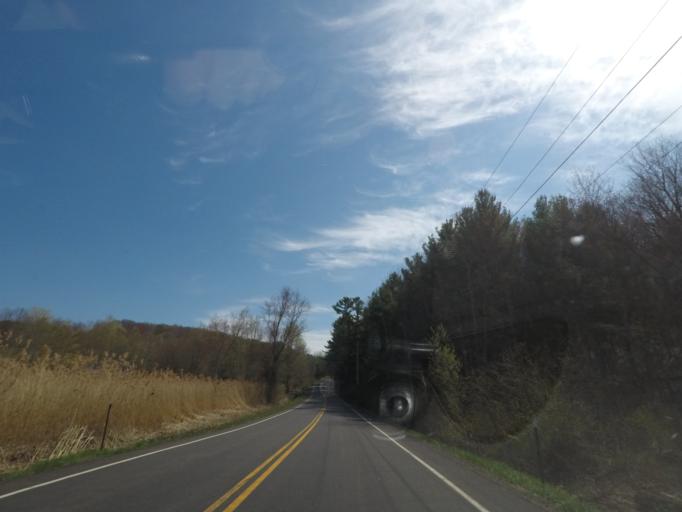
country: US
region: New York
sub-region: Columbia County
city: Chatham
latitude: 42.3790
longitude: -73.5299
